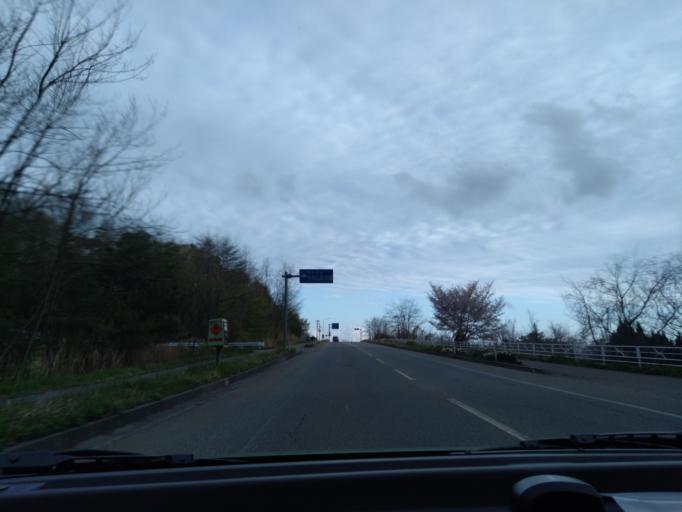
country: JP
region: Akita
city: Akita
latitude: 39.7391
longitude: 140.1366
